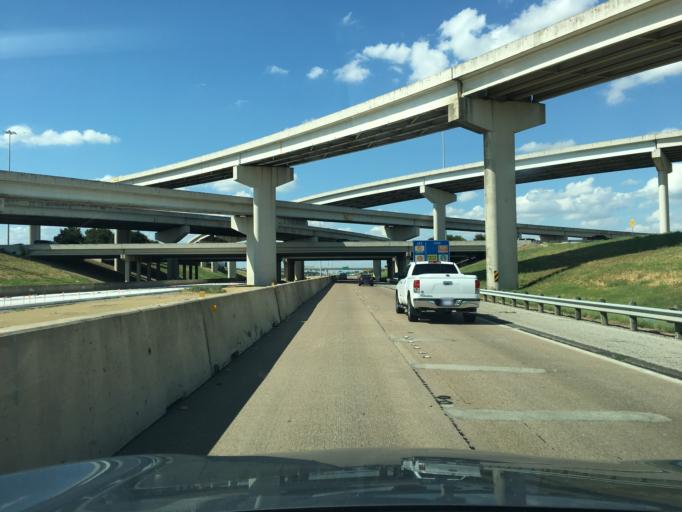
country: US
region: Texas
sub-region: Tarrant County
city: Arlington
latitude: 32.6760
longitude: -97.0625
